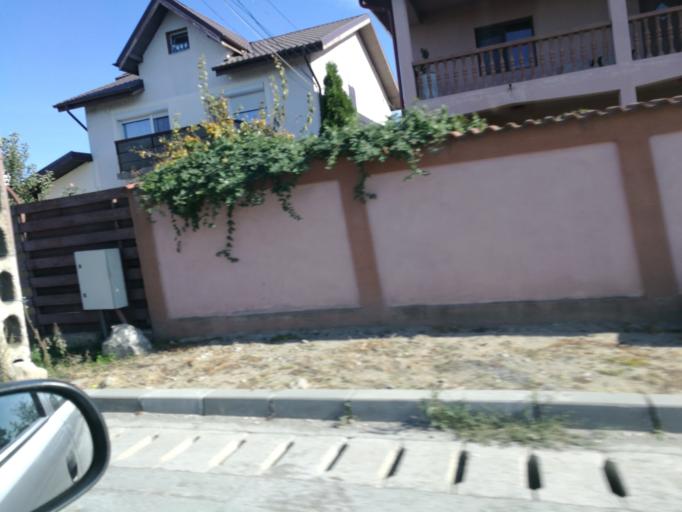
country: RO
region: Giurgiu
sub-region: Comuna Joita
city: Bacu
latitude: 44.4805
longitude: 25.8942
